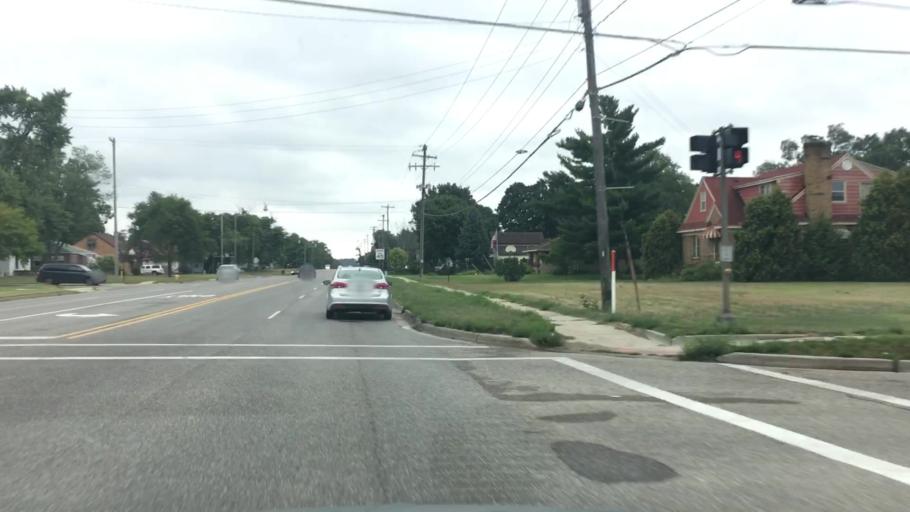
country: US
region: Michigan
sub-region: Ottawa County
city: Jenison
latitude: 42.9071
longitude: -85.8119
